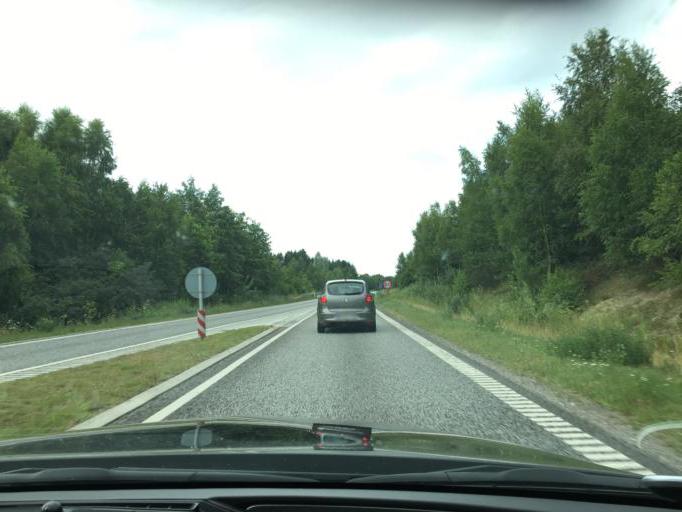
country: DK
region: Capital Region
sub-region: Gribskov Kommune
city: Helsinge
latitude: 55.9972
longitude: 12.2415
